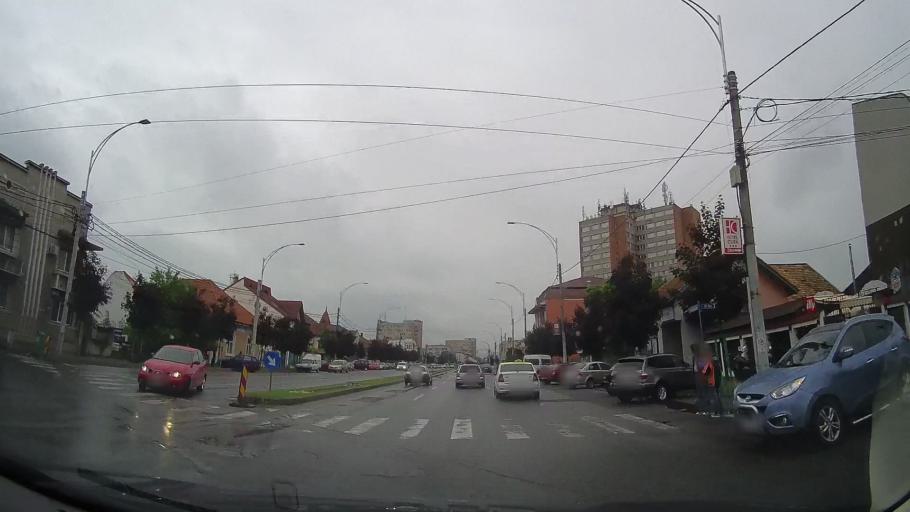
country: RO
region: Mehedinti
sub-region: Municipiul Drobeta-Turnu Severin
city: Drobeta-Turnu Severin
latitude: 44.6322
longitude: 22.6541
